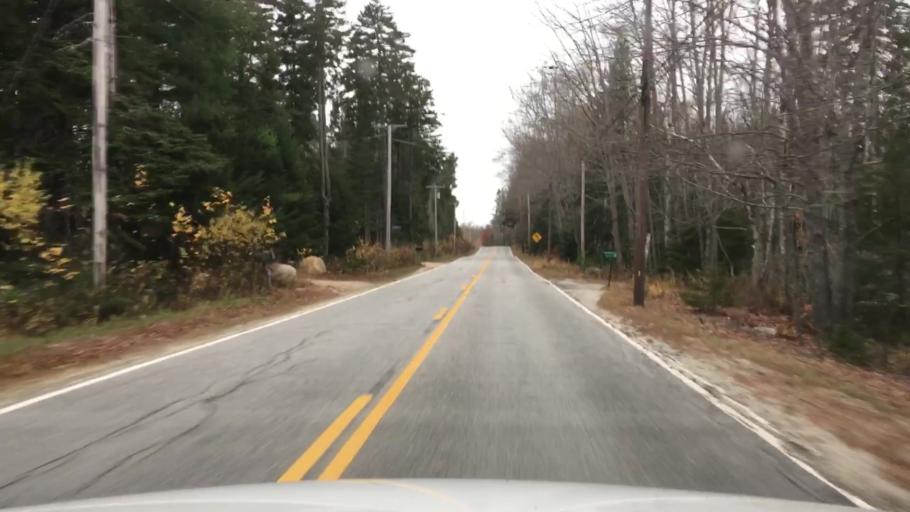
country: US
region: Maine
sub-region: Hancock County
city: Sedgwick
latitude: 44.2986
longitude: -68.5585
